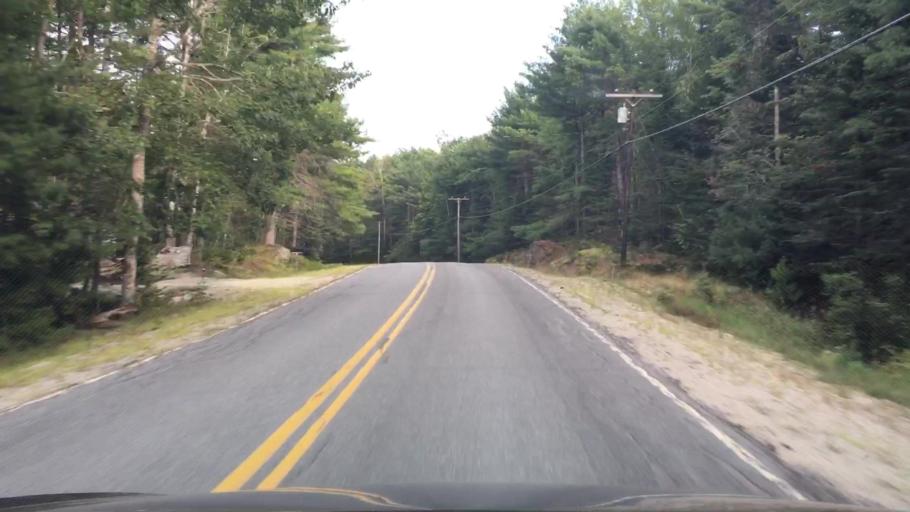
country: US
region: Maine
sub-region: Hancock County
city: Surry
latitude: 44.4979
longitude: -68.5432
